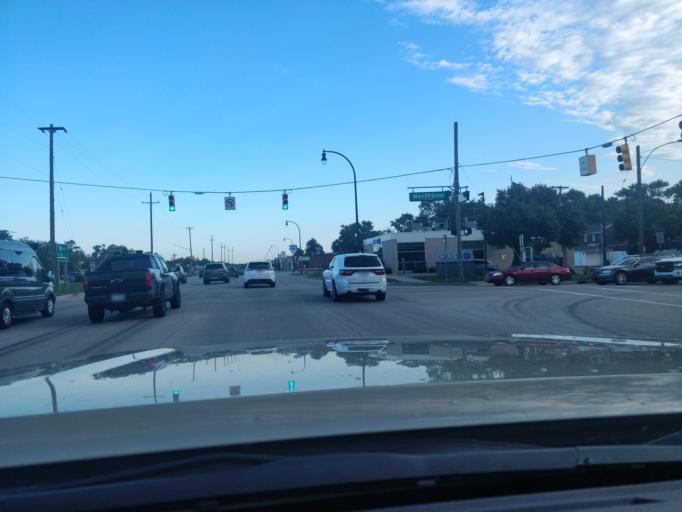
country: US
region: Michigan
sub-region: Wayne County
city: Southgate
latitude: 42.2135
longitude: -83.1807
